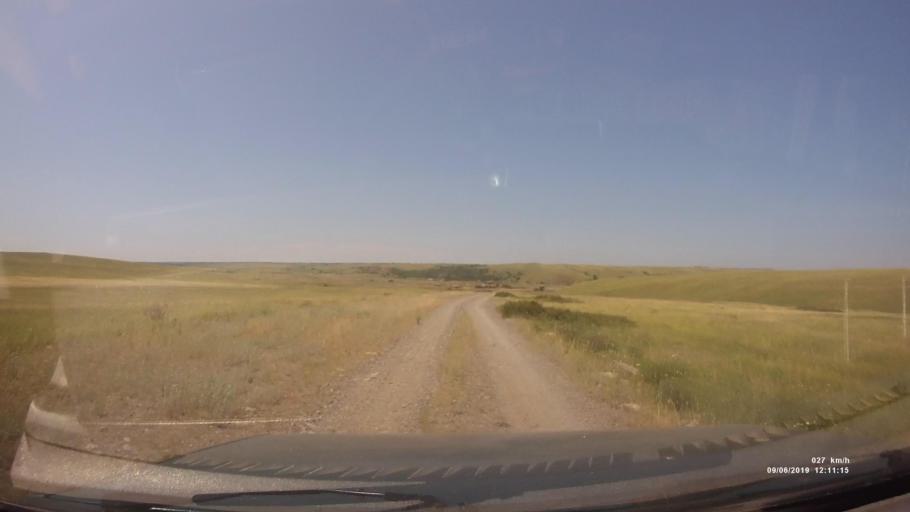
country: RU
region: Rostov
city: Staraya Stanitsa
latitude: 48.2502
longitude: 40.3347
